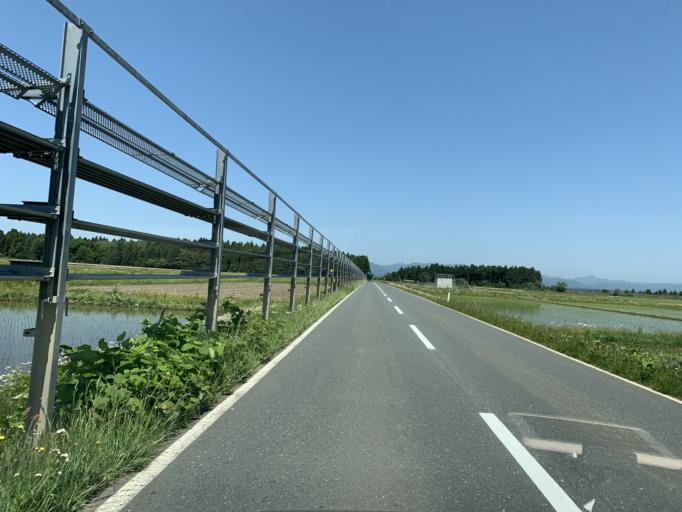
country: JP
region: Iwate
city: Kitakami
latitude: 39.2724
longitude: 141.0540
